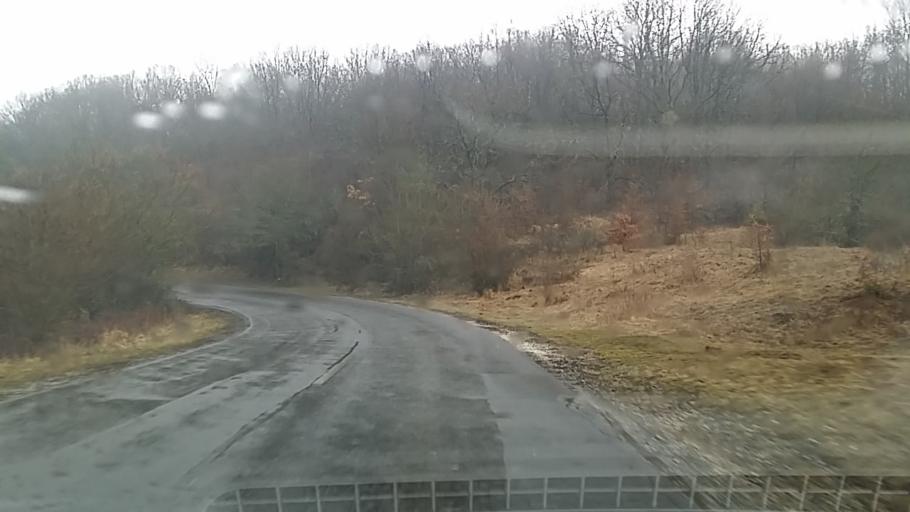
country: HU
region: Borsod-Abauj-Zemplen
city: Rudabanya
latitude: 48.4675
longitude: 20.5268
